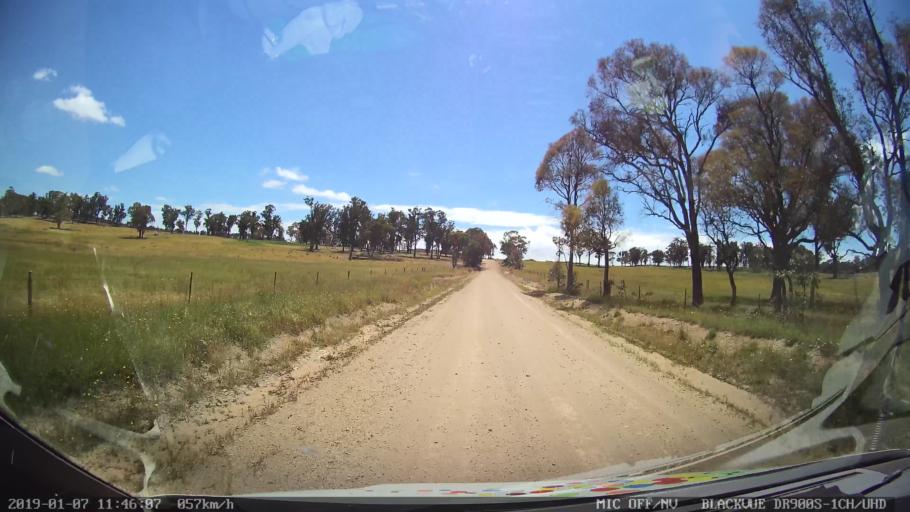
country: AU
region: New South Wales
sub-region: Guyra
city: Guyra
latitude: -30.3439
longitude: 151.6111
